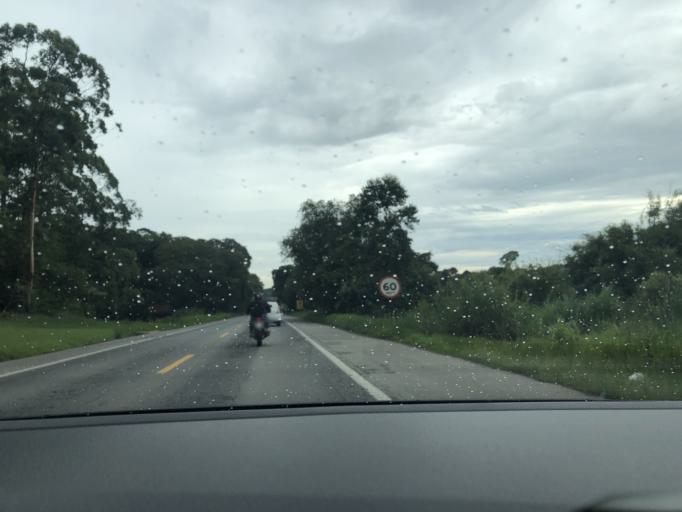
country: BR
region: Sao Paulo
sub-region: Jarinu
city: Jarinu
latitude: -23.1212
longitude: -46.7312
